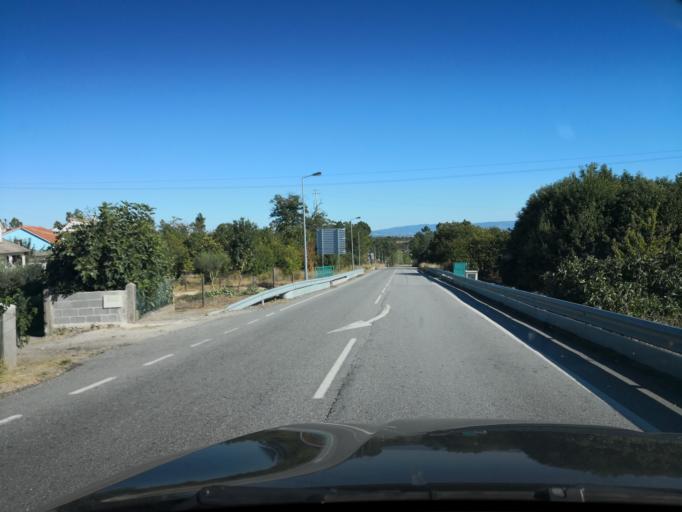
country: PT
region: Vila Real
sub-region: Valpacos
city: Valpacos
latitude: 41.6593
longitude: -7.3268
